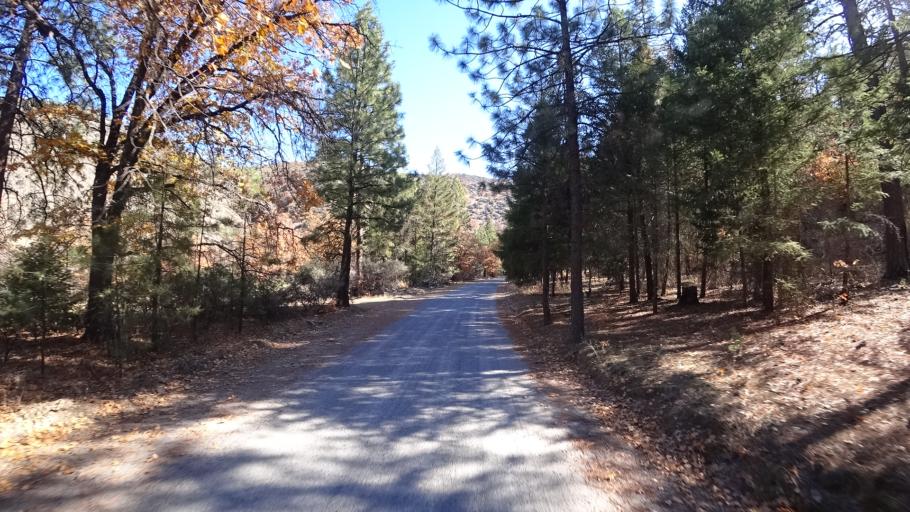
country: US
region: California
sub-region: Siskiyou County
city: Yreka
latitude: 41.8541
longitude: -122.6981
